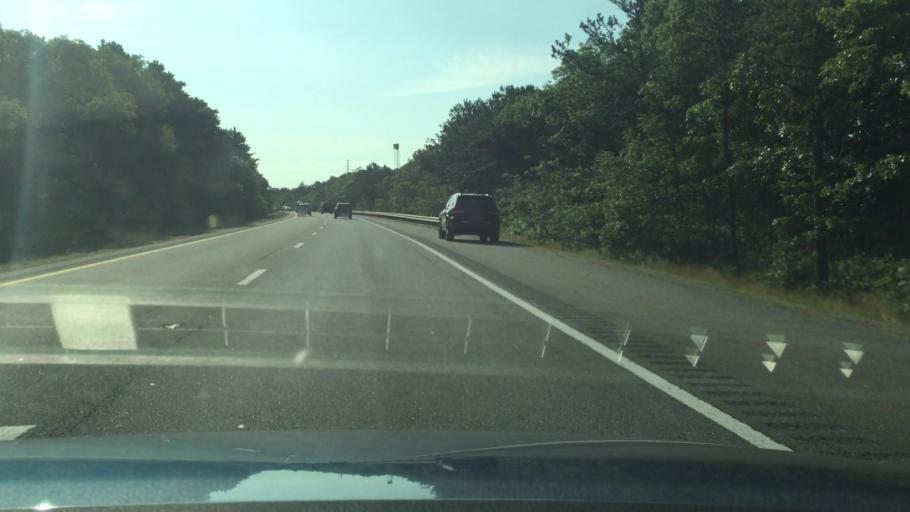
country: US
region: Massachusetts
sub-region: Barnstable County
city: Barnstable
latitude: 41.6872
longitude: -70.3016
